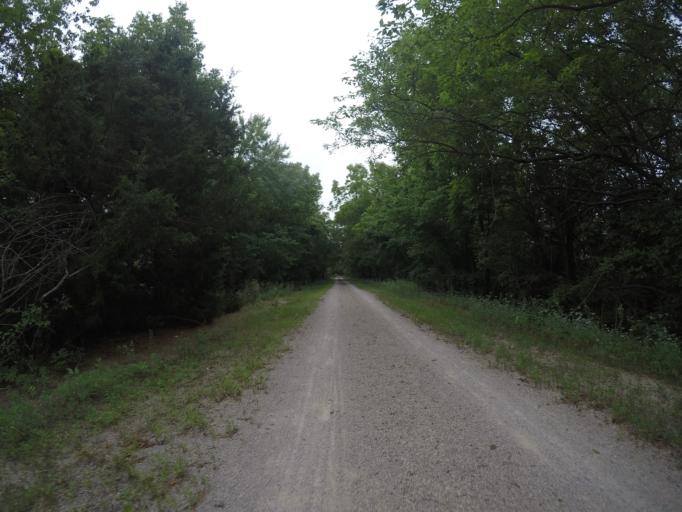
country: US
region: Kansas
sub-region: Franklin County
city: Ottawa
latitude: 38.5574
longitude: -95.2714
